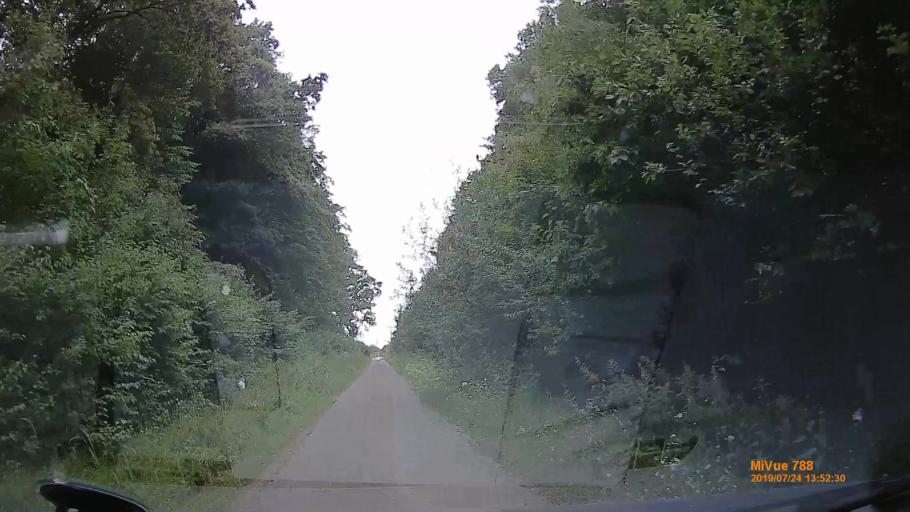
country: HU
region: Szabolcs-Szatmar-Bereg
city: Aranyosapati
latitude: 48.2643
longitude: 22.3357
